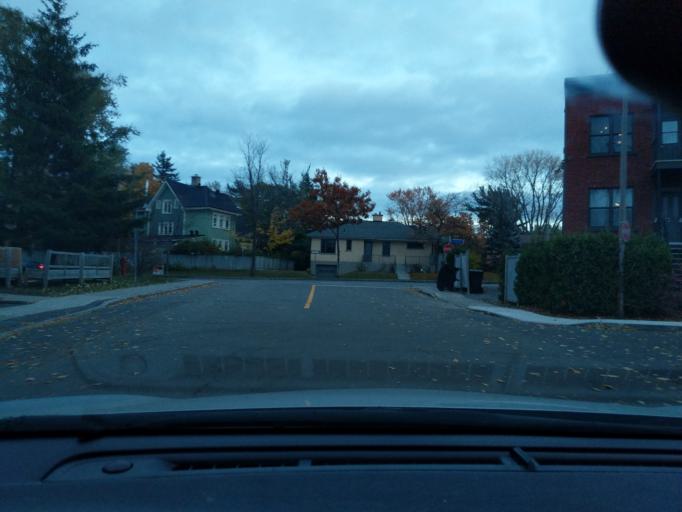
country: CA
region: Quebec
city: Quebec
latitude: 46.7882
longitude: -71.2492
